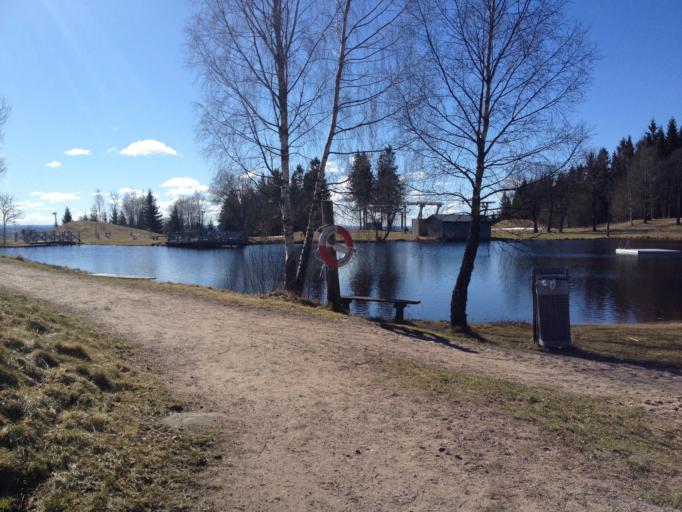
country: SE
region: Vaestra Goetaland
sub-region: Falkopings Kommun
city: Falkoeping
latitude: 58.1747
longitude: 13.5232
